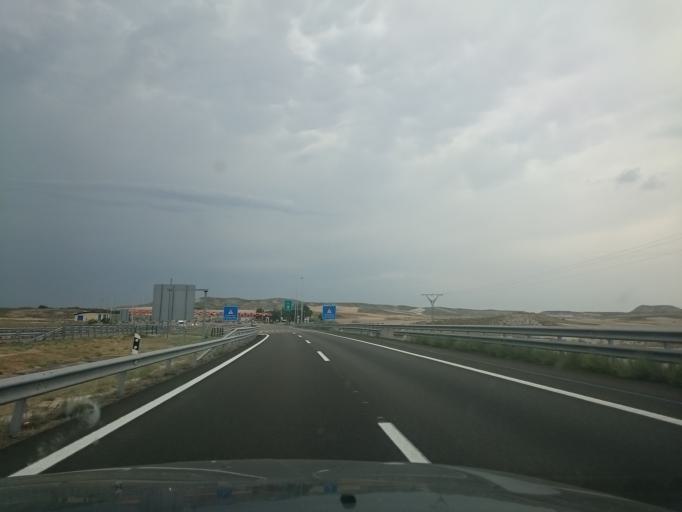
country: ES
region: Aragon
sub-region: Provincia de Zaragoza
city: Pina de Ebro
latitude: 41.5257
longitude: -0.4631
